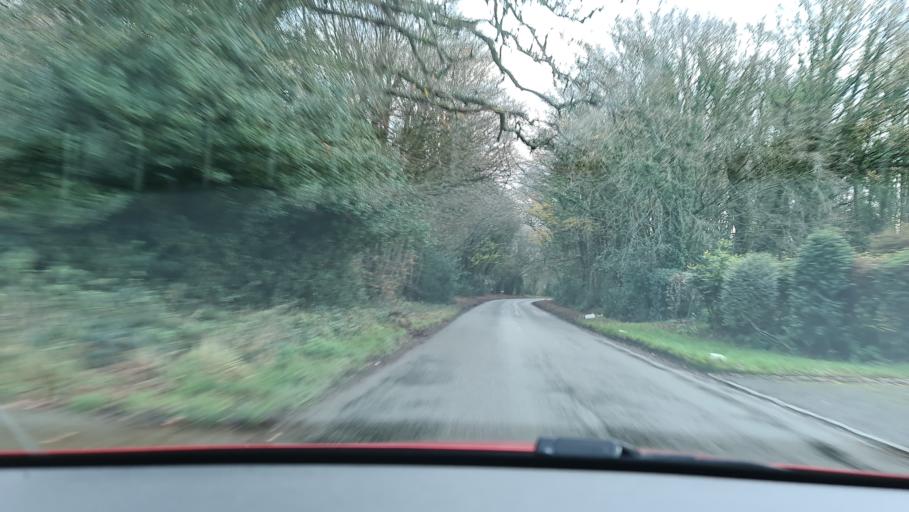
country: GB
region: England
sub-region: Buckinghamshire
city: Great Missenden
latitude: 51.7381
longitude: -0.6911
